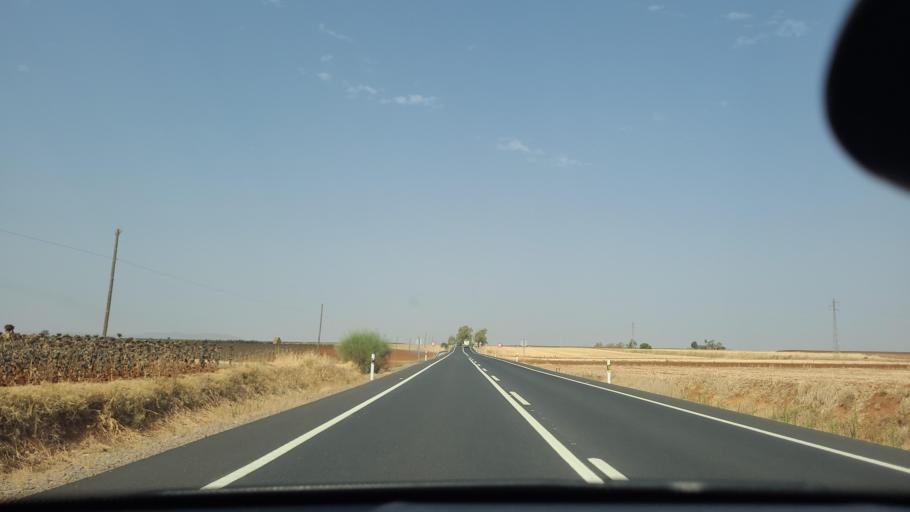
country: ES
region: Extremadura
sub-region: Provincia de Badajoz
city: Berlanga
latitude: 38.2653
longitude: -5.7559
